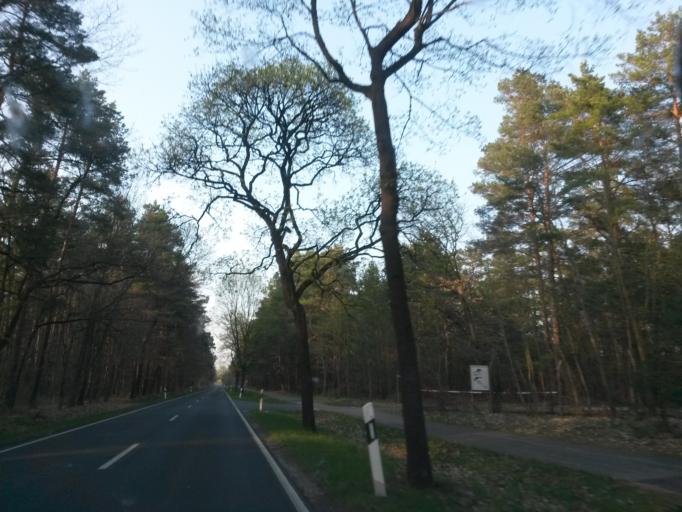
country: DE
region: Brandenburg
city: Rehfelde
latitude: 52.4728
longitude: 13.9084
